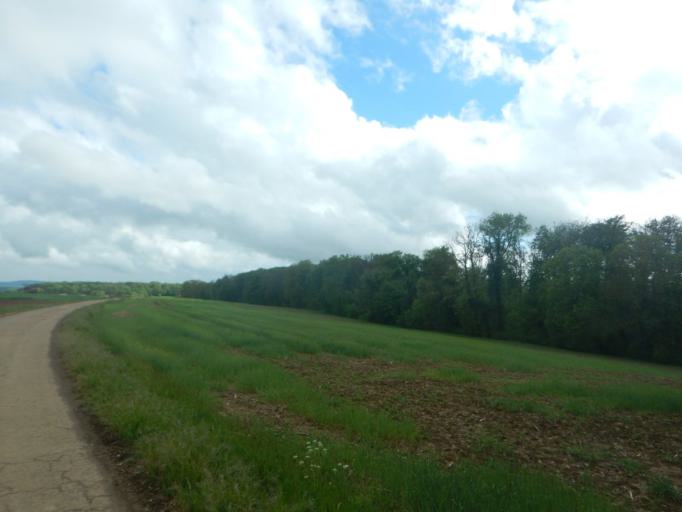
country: LU
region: Luxembourg
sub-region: Canton d'Esch-sur-Alzette
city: Reckange-sur-Mess
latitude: 49.5551
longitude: 6.0003
